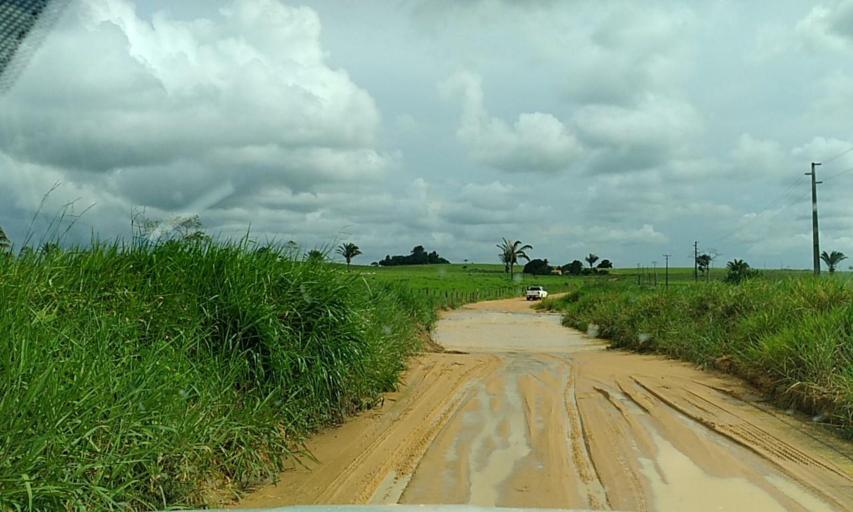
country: BR
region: Para
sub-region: Altamira
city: Altamira
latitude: -3.2475
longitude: -52.6945
